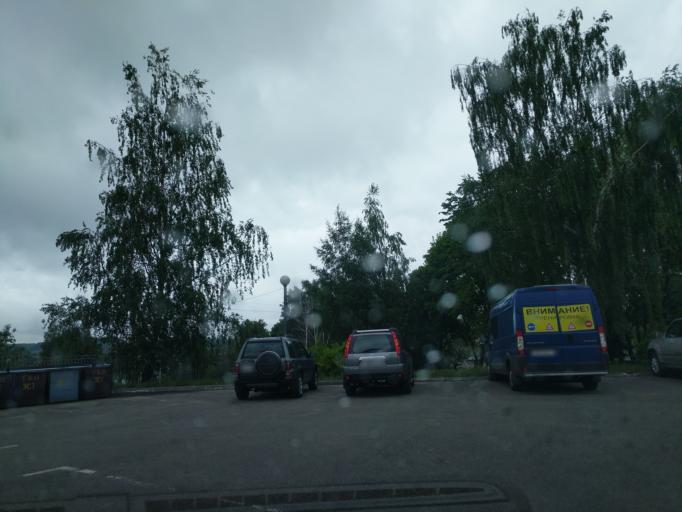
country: BY
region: Minsk
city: Khatsyezhyna
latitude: 53.9360
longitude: 27.3522
